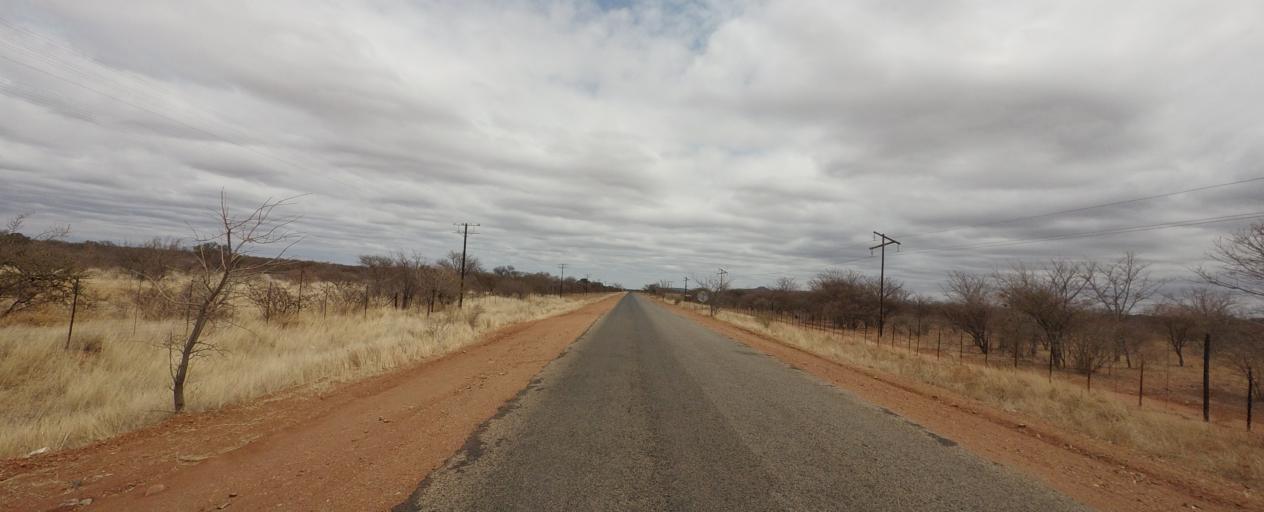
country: BW
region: Central
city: Mathathane
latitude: -22.6767
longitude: 29.0950
